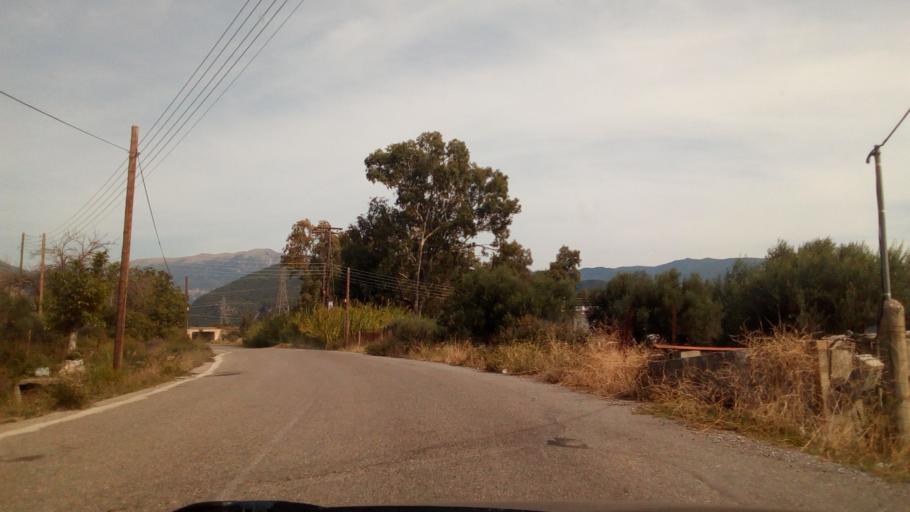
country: GR
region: West Greece
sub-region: Nomos Aitolias kai Akarnanias
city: Nafpaktos
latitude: 38.4050
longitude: 21.8798
